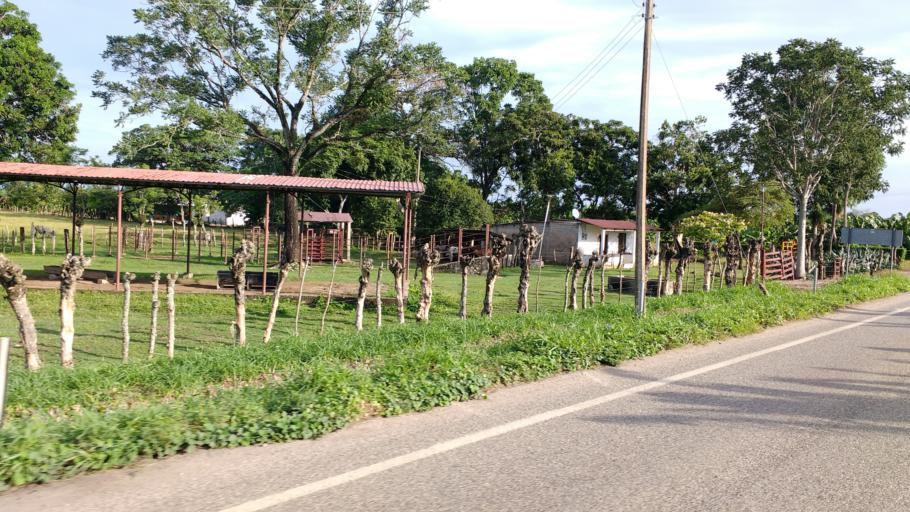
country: MX
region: Tabasco
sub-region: Teapa
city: Eureka y Belen
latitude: 17.6185
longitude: -92.9634
